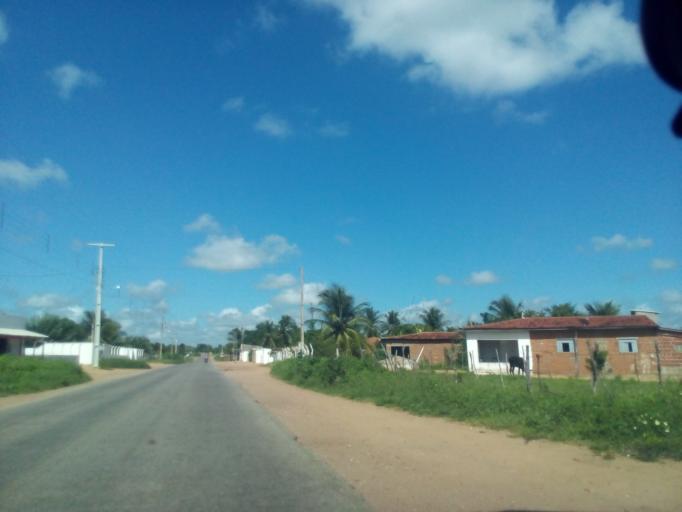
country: BR
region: Rio Grande do Norte
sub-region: Sao Paulo Do Potengi
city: Sao Paulo do Potengi
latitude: -5.9133
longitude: -35.7050
